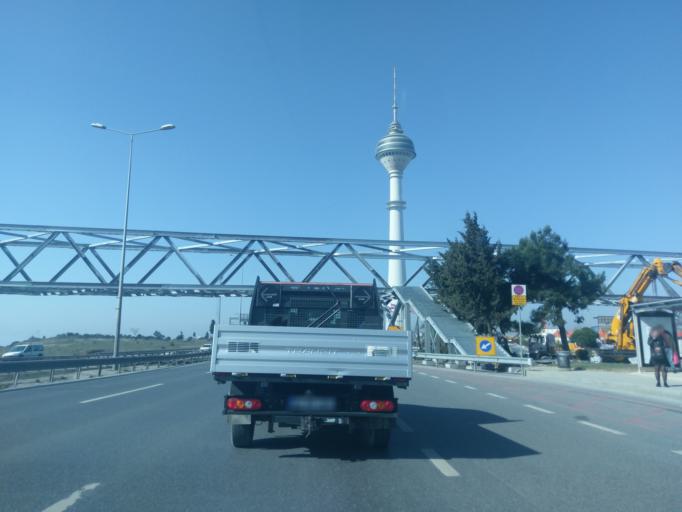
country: TR
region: Istanbul
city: Gurpinar
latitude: 41.0237
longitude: 28.6237
